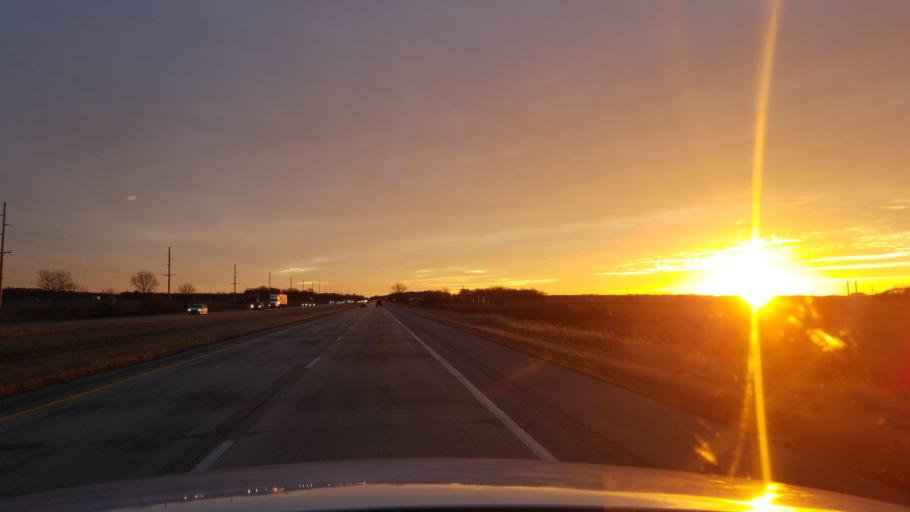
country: US
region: Indiana
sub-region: Posey County
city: Mount Vernon
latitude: 37.9421
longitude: -87.7793
